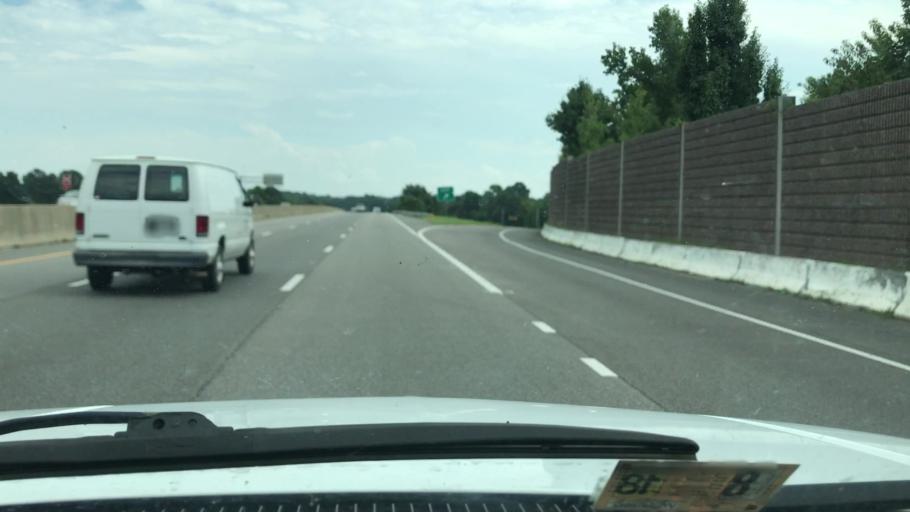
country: US
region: Virginia
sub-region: Chesterfield County
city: Bon Air
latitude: 37.4811
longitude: -77.5164
